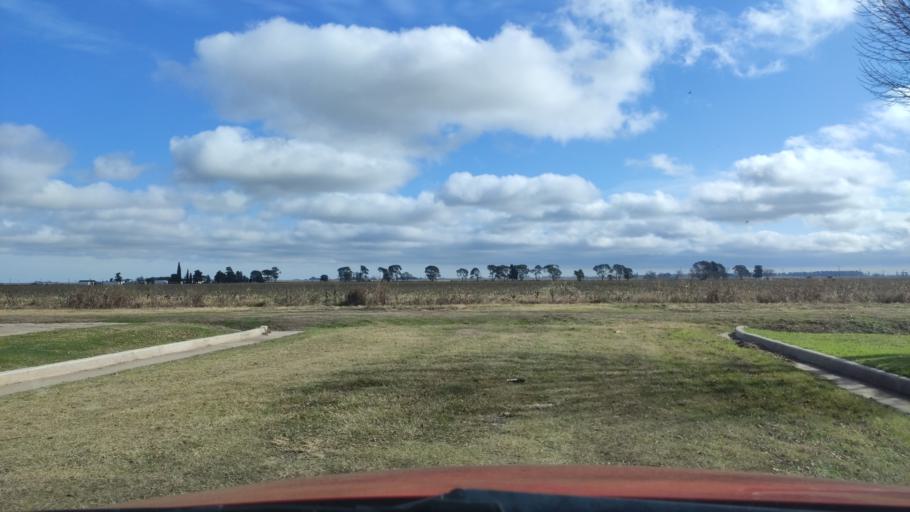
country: AR
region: Cordoba
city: General Roca
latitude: -32.7330
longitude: -61.9229
